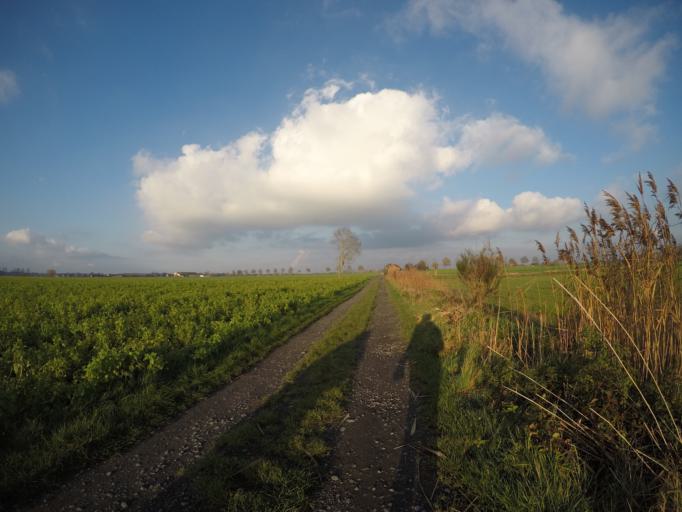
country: BE
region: Flanders
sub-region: Provincie West-Vlaanderen
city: Lichtervelde
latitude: 51.0625
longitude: 3.1722
